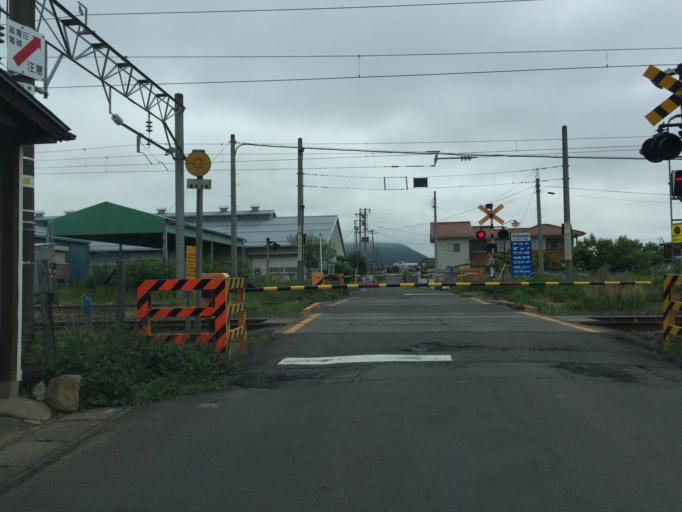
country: JP
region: Fukushima
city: Fukushima-shi
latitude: 37.7710
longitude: 140.3929
